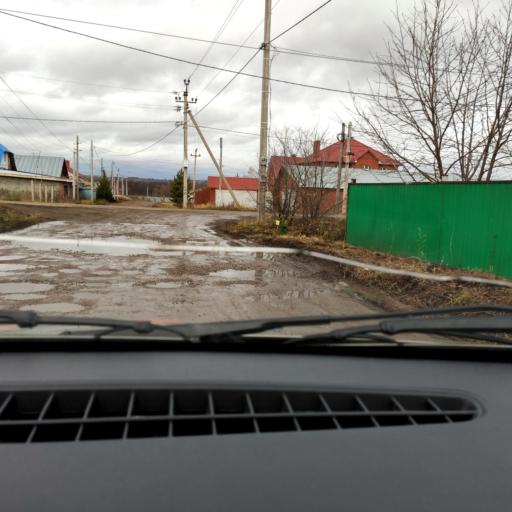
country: RU
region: Bashkortostan
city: Avdon
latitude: 54.4893
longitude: 55.8581
